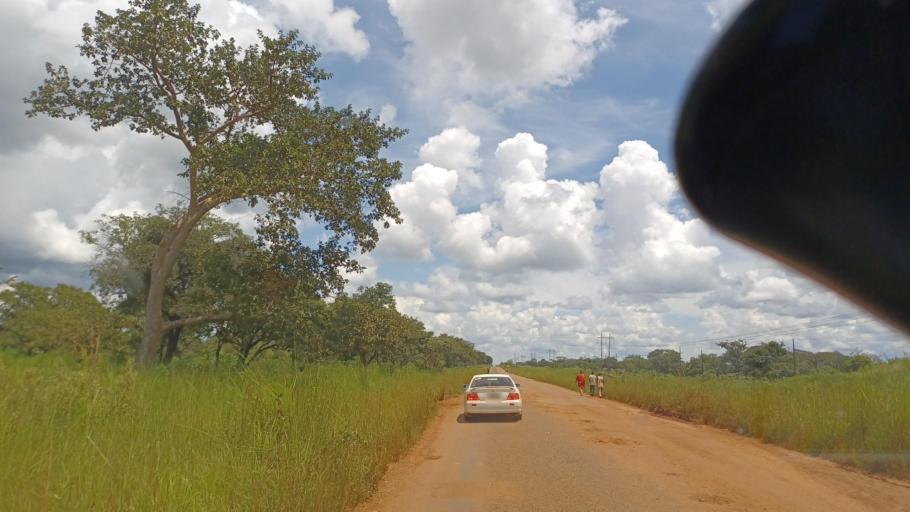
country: ZM
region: North-Western
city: Solwezi
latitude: -12.4841
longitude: 26.1959
